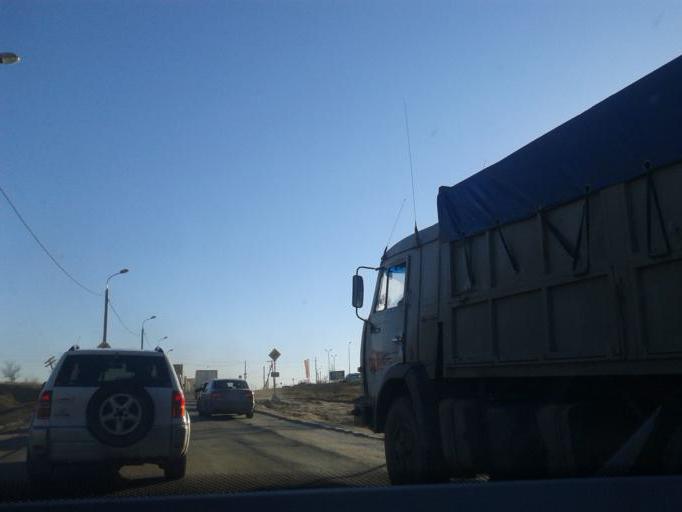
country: RU
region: Volgograd
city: Volgograd
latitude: 48.7059
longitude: 44.4405
